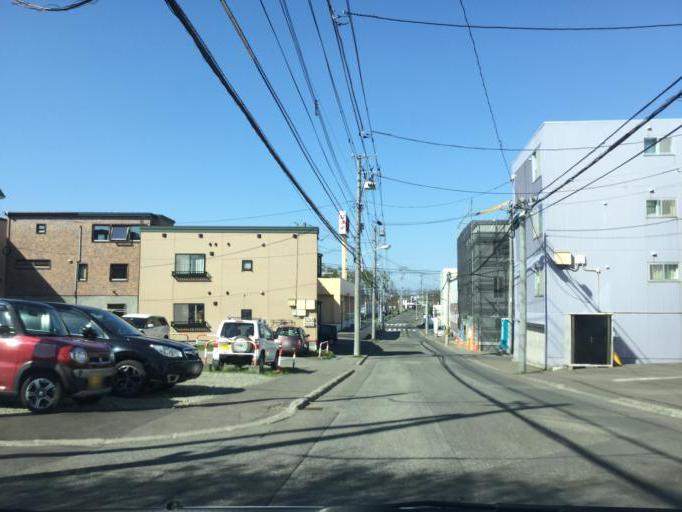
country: JP
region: Hokkaido
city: Sapporo
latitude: 43.0164
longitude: 141.4221
